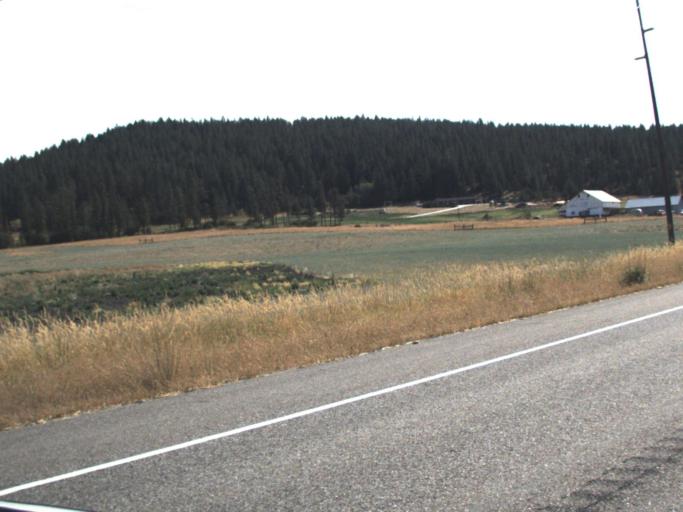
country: US
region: Washington
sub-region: Stevens County
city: Chewelah
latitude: 48.2150
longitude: -117.7154
